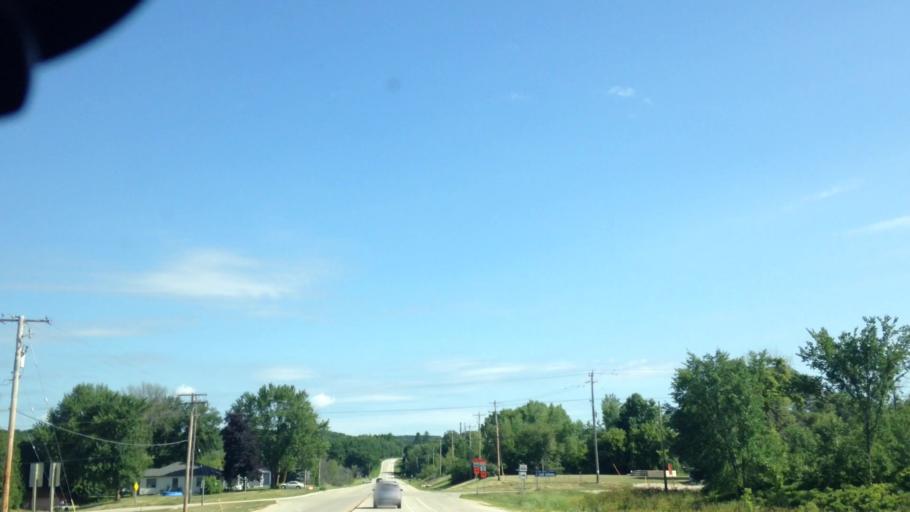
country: US
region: Wisconsin
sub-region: Washington County
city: Slinger
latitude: 43.3524
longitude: -88.2806
